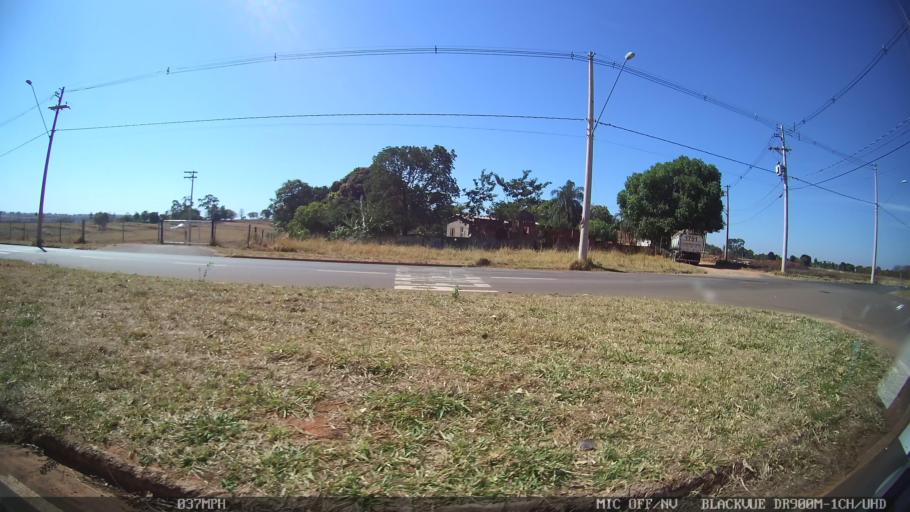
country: BR
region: Sao Paulo
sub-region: Sao Jose Do Rio Preto
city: Sao Jose do Rio Preto
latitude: -20.7326
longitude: -49.4366
